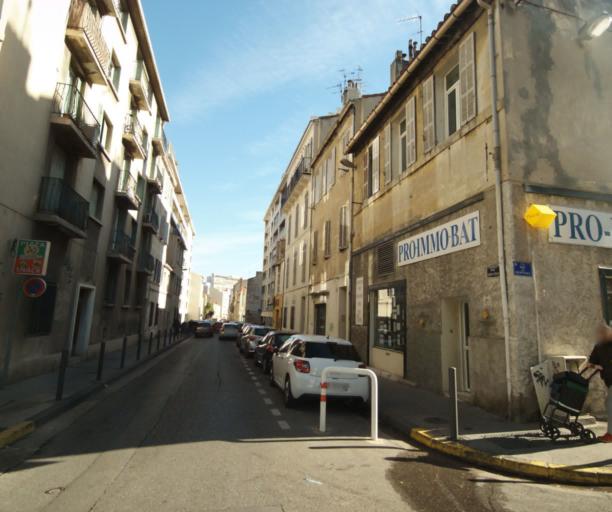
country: FR
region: Provence-Alpes-Cote d'Azur
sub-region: Departement des Bouches-du-Rhone
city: Marseille 05
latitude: 43.2882
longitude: 5.3952
